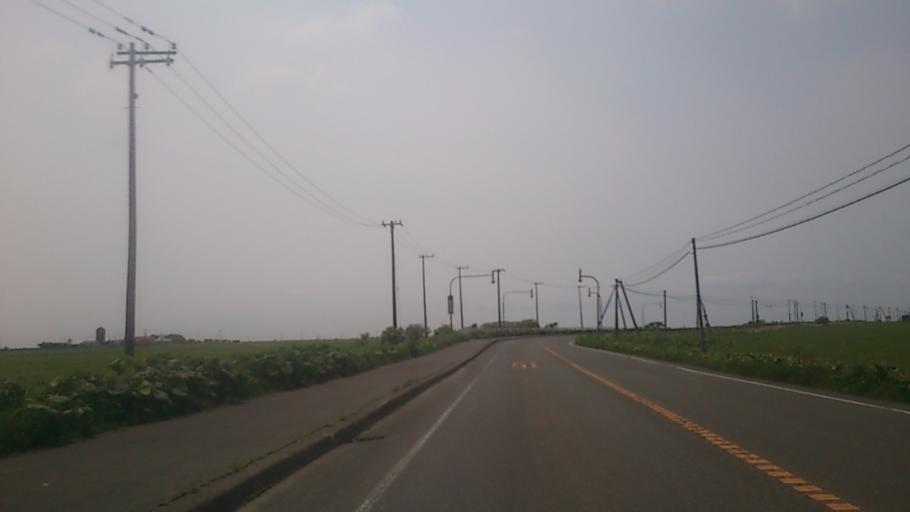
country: JP
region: Hokkaido
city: Nemuro
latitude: 43.2719
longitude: 145.5366
